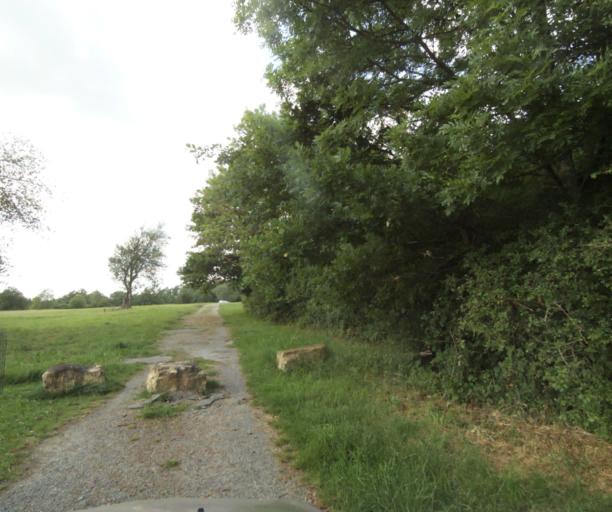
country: FR
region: Champagne-Ardenne
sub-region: Departement des Ardennes
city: Montcy-Notre-Dame
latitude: 49.7637
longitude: 4.7379
